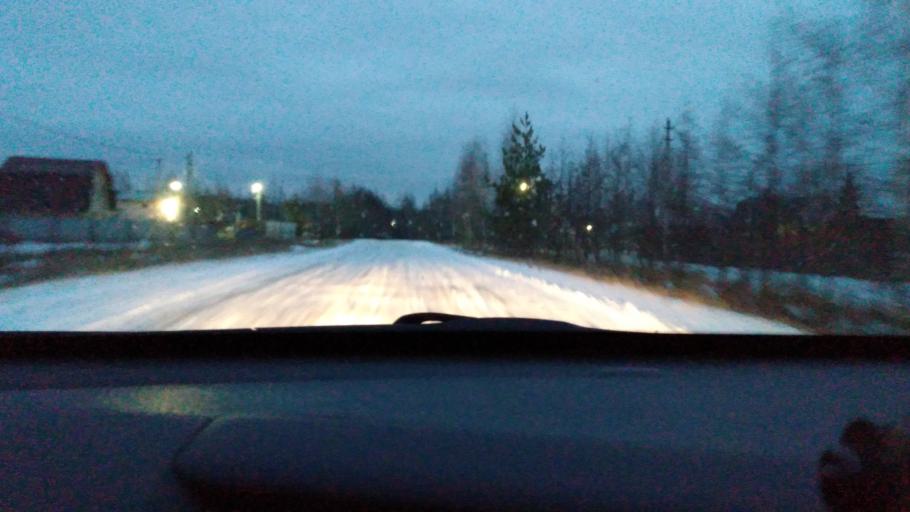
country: RU
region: Moskovskaya
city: Meshcherino
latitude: 55.3230
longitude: 38.3461
